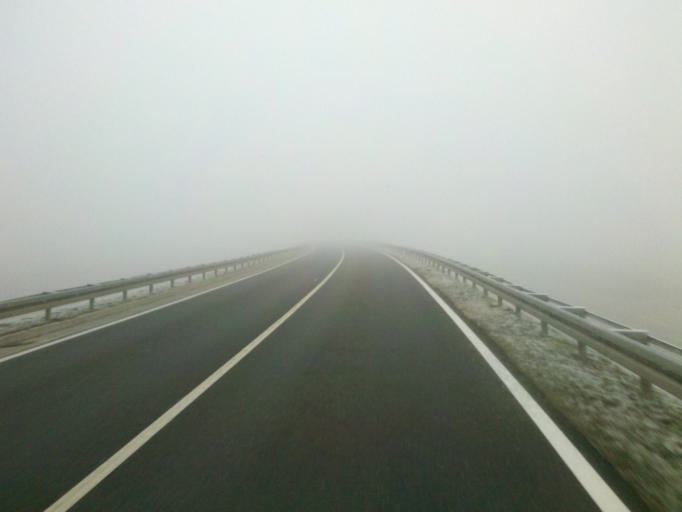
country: HR
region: Varazdinska
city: Jalkovec
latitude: 46.2866
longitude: 16.3113
